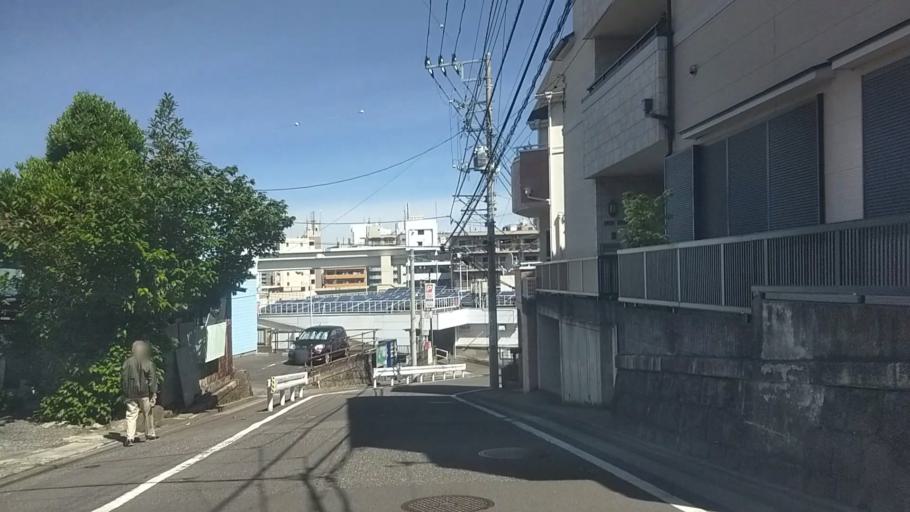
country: JP
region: Kanagawa
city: Yokohama
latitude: 35.4354
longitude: 139.6363
